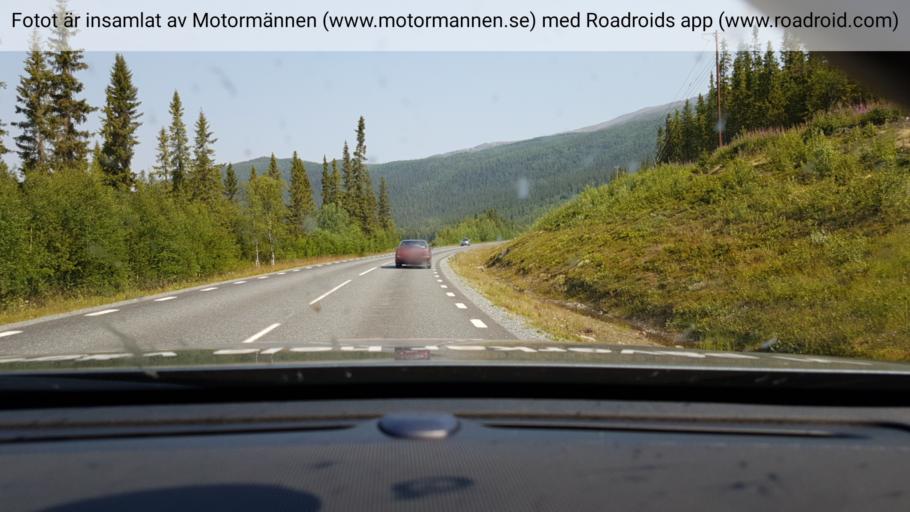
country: SE
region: Vaesterbotten
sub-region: Vilhelmina Kommun
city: Sjoberg
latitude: 65.6209
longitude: 15.5353
